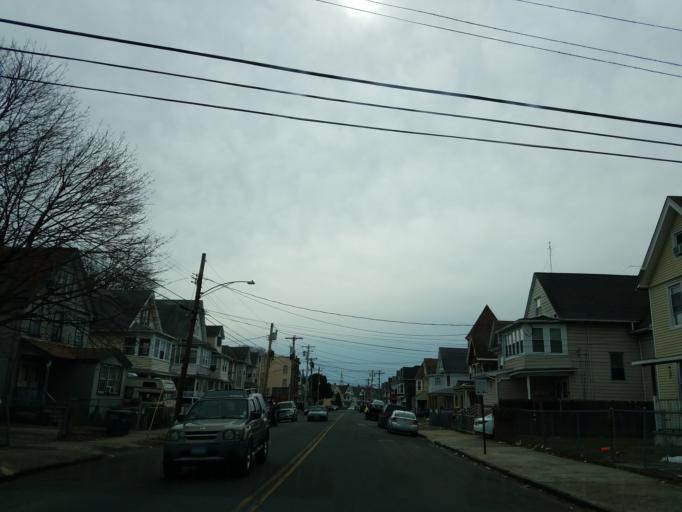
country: US
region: Connecticut
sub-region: Fairfield County
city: Bridgeport
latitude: 41.1786
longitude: -73.2034
